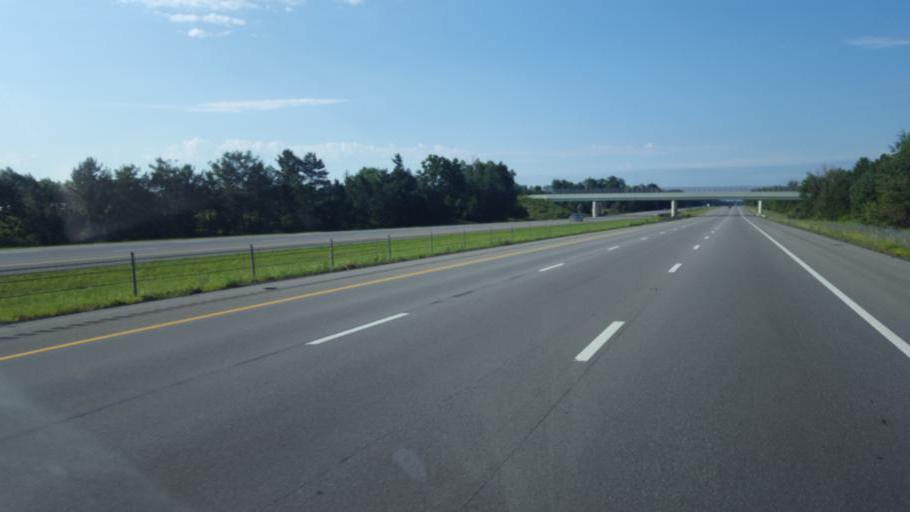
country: US
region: Ohio
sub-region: Morrow County
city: Cardington
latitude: 40.4026
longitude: -82.8227
